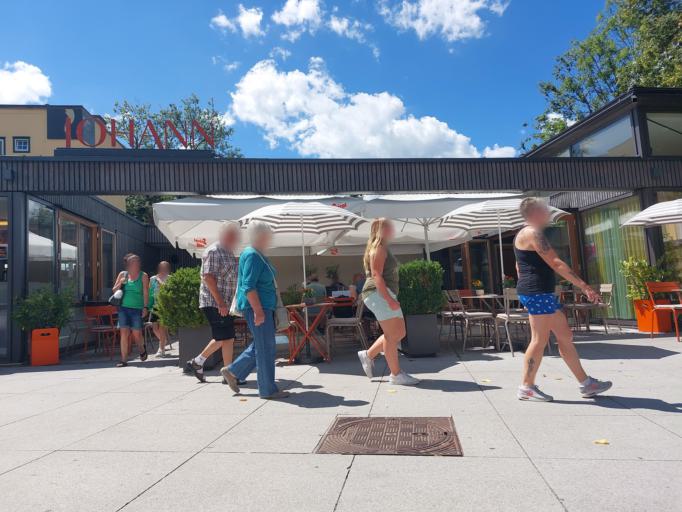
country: AT
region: Upper Austria
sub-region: Politischer Bezirk Gmunden
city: Bad Ischl
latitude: 47.7109
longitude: 13.6208
